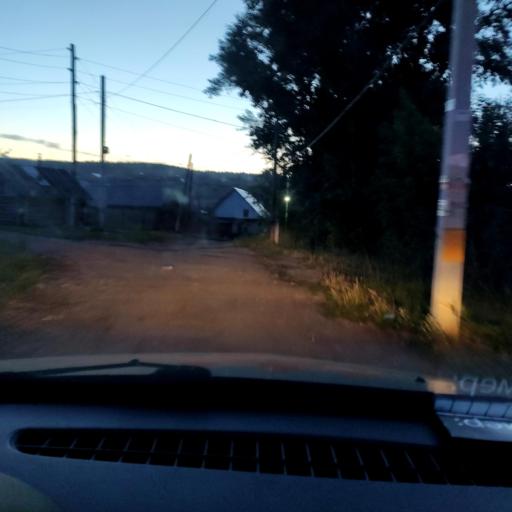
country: RU
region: Bashkortostan
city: Iglino
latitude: 54.8368
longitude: 56.4090
